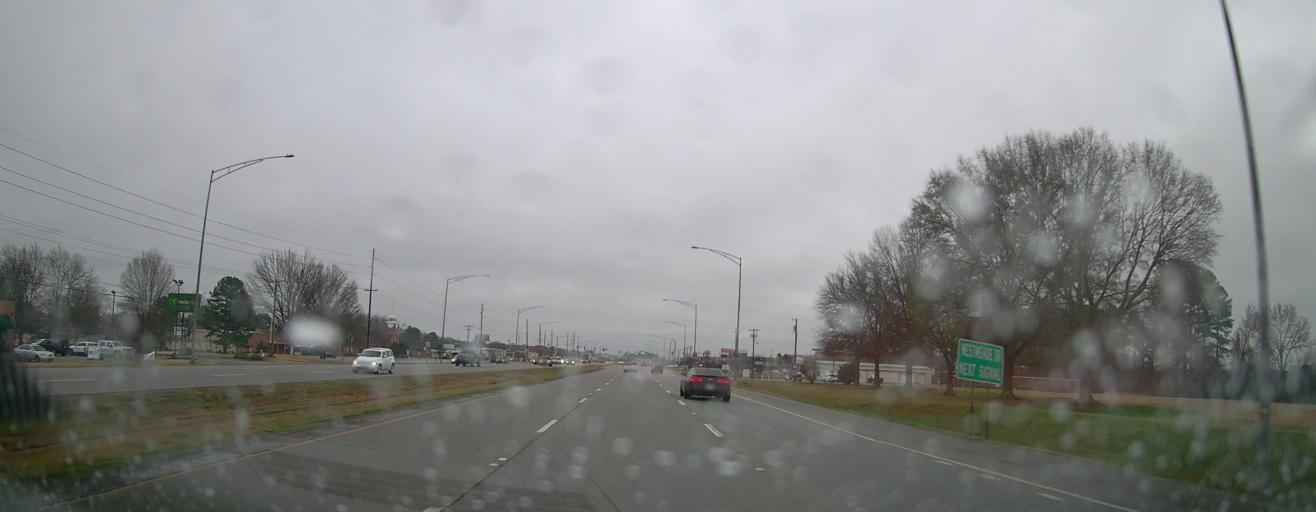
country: US
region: Alabama
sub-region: Morgan County
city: Decatur
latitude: 34.5826
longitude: -87.0229
